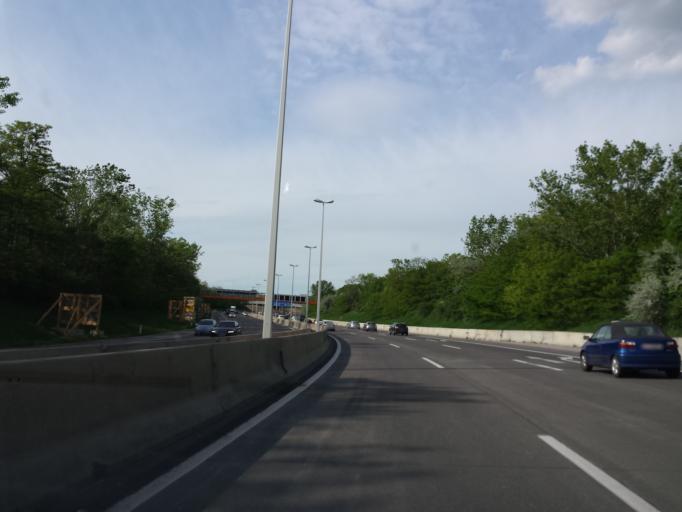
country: AT
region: Lower Austria
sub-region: Politischer Bezirk Wien-Umgebung
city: Leopoldsdorf
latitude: 48.1526
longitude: 16.3746
